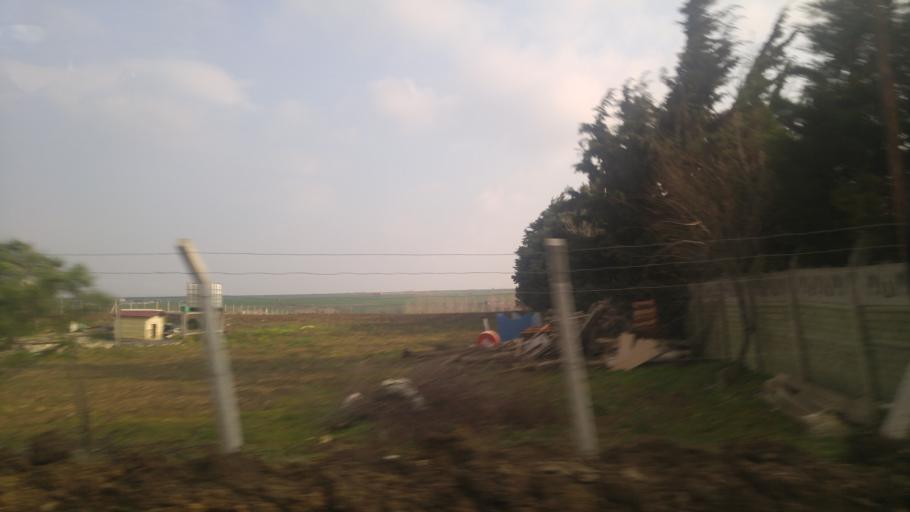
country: TR
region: Istanbul
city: Silivri
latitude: 41.0941
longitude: 28.2761
